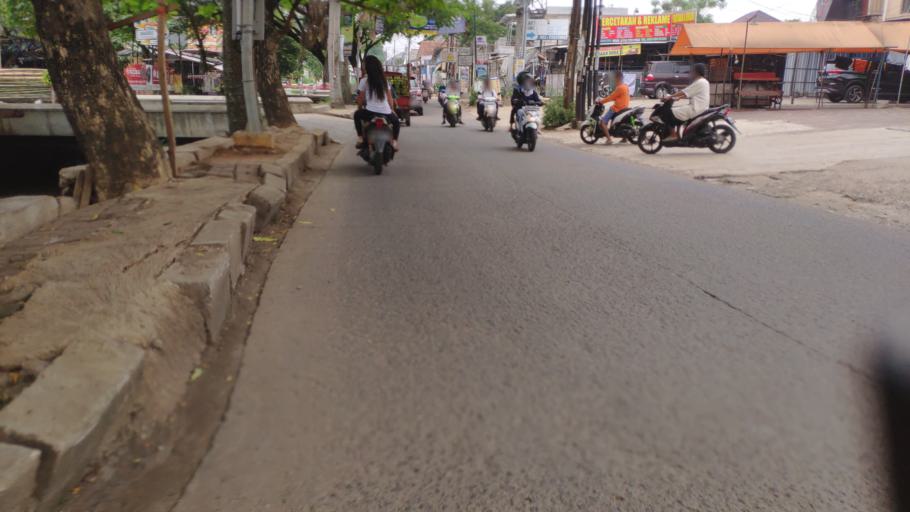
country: ID
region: West Java
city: Sawangan
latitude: -6.3857
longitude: 106.7913
